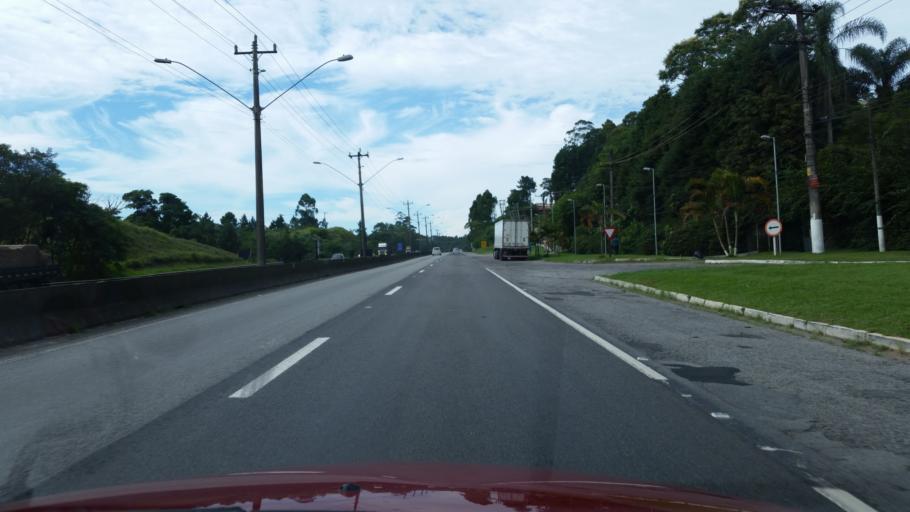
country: BR
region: Sao Paulo
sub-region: Itapecerica Da Serra
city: Itapecerica da Serra
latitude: -23.7493
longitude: -46.9010
